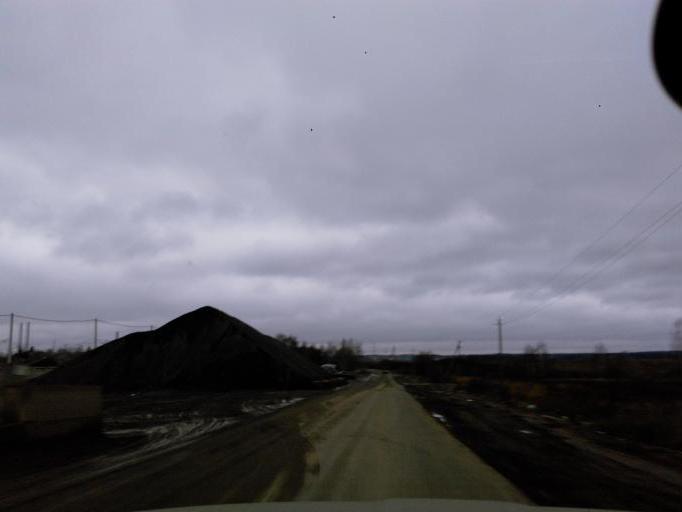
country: RU
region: Moskovskaya
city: Radumlya
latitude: 56.0575
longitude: 37.1362
